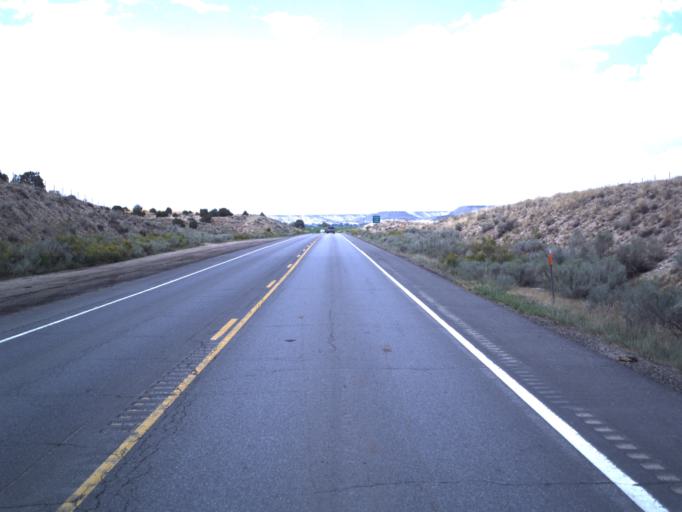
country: US
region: Utah
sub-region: Duchesne County
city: Duchesne
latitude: 40.1671
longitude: -110.2934
